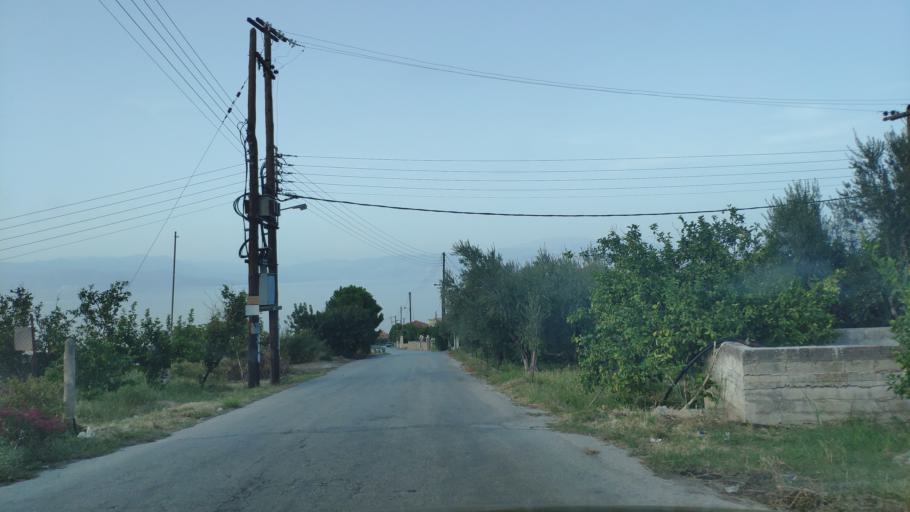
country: GR
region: West Greece
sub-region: Nomos Achaias
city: Aiyira
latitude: 38.1233
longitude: 22.3989
